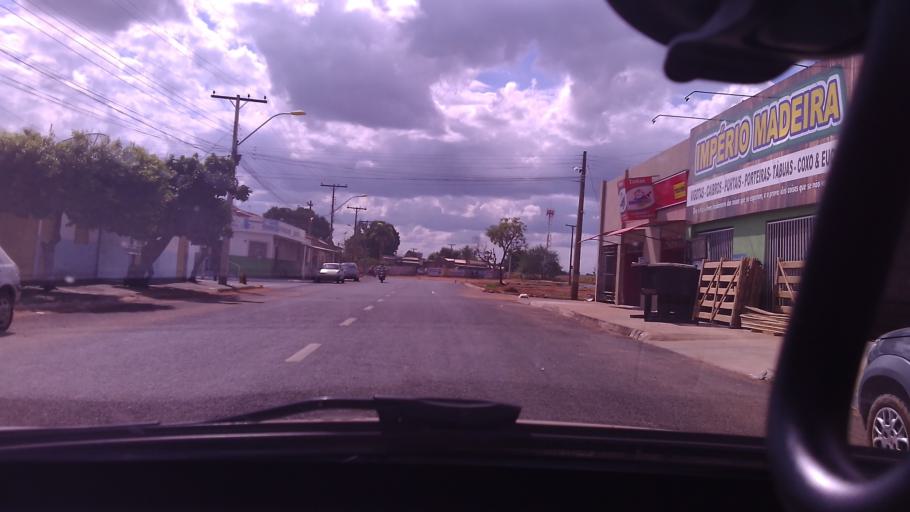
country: BR
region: Goias
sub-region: Mineiros
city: Mineiros
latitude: -17.5399
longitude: -52.5416
